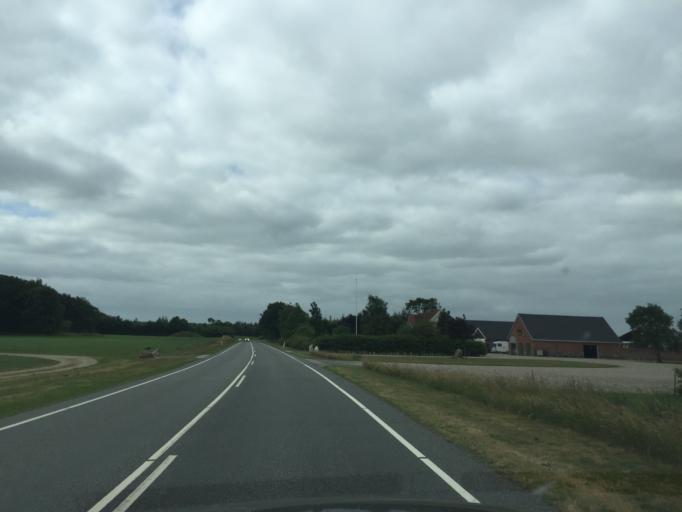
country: DK
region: South Denmark
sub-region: Vejen Kommune
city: Brorup
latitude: 55.4227
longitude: 8.9571
